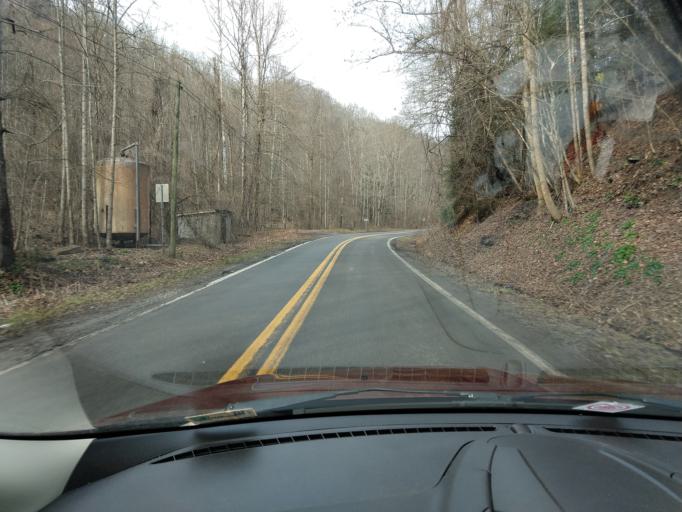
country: US
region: West Virginia
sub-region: McDowell County
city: Welch
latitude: 37.3428
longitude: -81.6711
